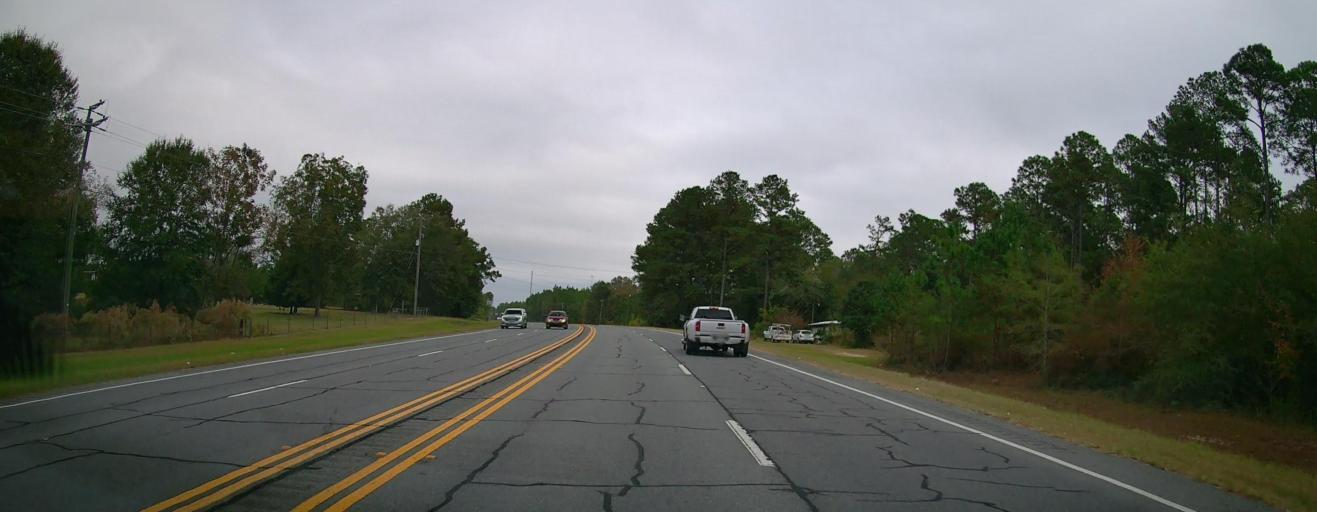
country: US
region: Georgia
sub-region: Tift County
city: Omega
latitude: 31.3065
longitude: -83.6389
